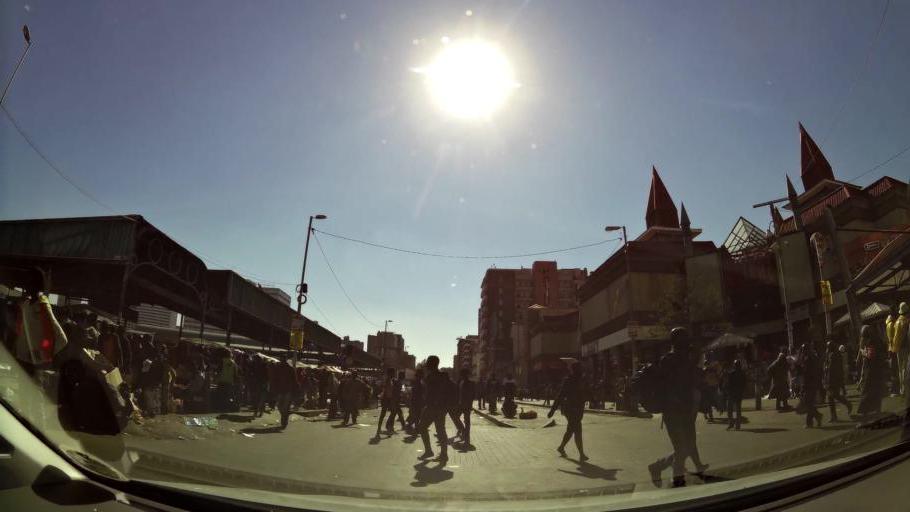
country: ZA
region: Gauteng
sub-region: City of Johannesburg Metropolitan Municipality
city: Johannesburg
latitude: -26.1983
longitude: 28.0448
